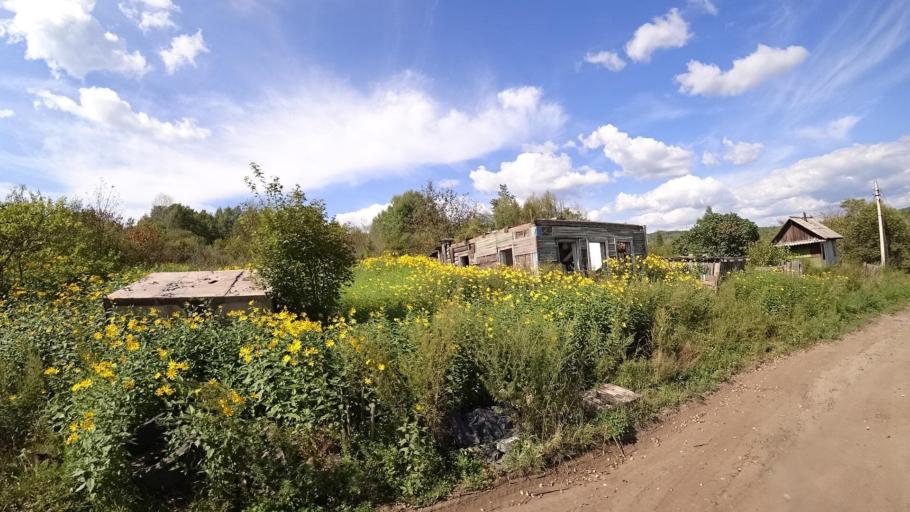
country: RU
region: Jewish Autonomous Oblast
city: Birakan
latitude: 49.0003
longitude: 131.8529
